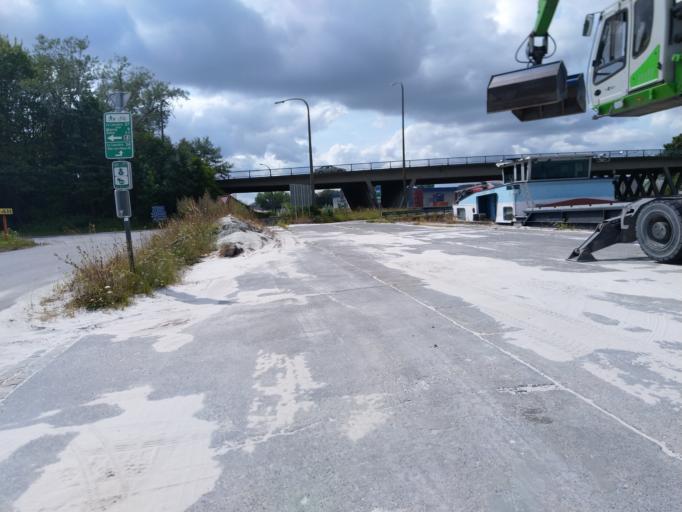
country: BE
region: Wallonia
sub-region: Province du Hainaut
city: Quaregnon
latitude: 50.4792
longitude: 3.8803
